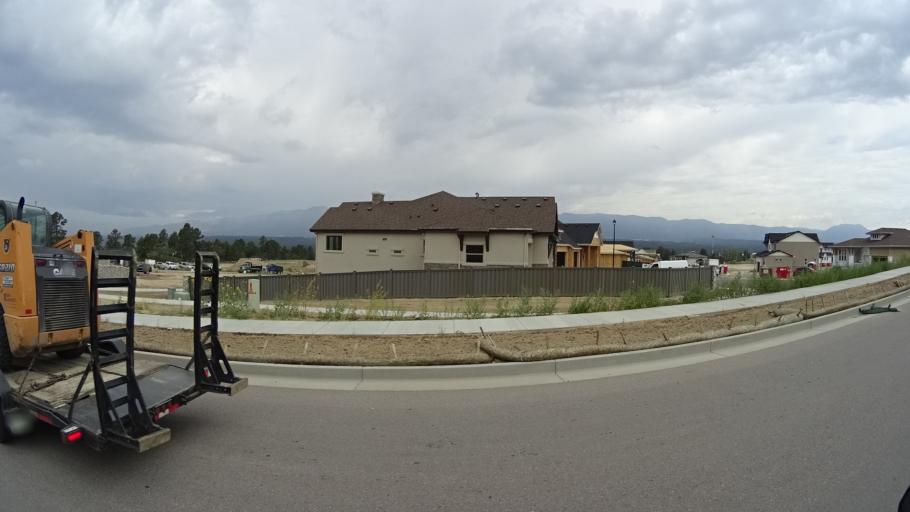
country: US
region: Colorado
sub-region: El Paso County
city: Gleneagle
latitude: 39.0040
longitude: -104.8118
